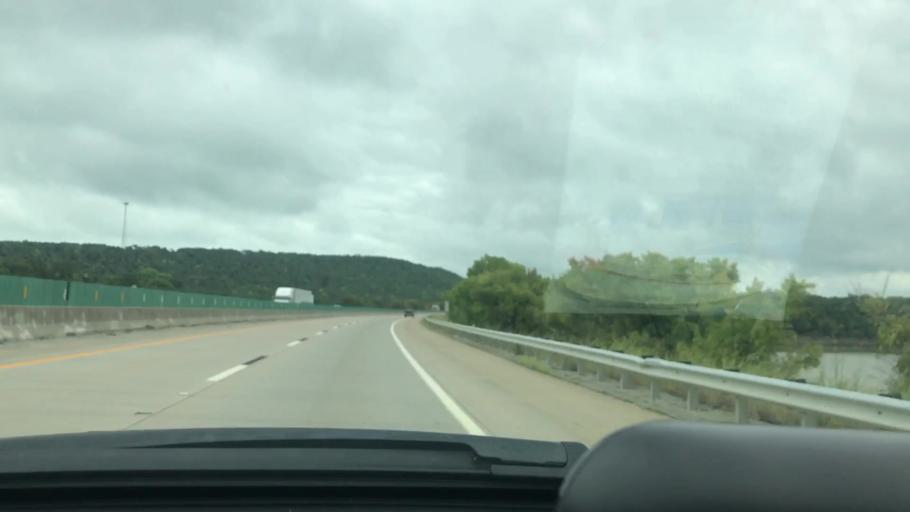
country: US
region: Oklahoma
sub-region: Pittsburg County
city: Krebs
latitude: 35.1080
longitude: -95.6937
